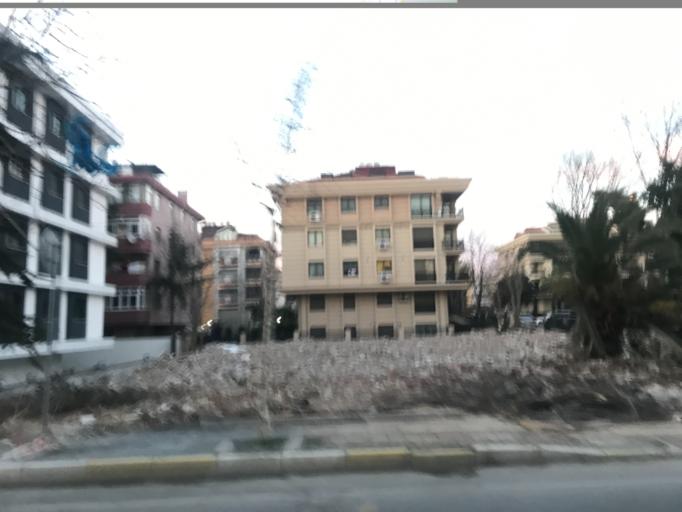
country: TR
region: Istanbul
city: Bahcelievler
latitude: 40.9606
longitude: 28.8350
